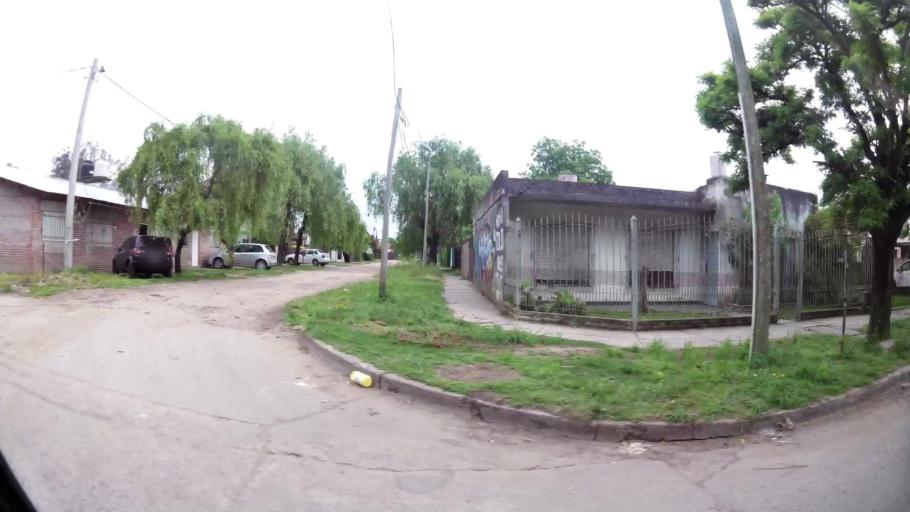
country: AR
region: Buenos Aires
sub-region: Partido de Ezeiza
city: Ezeiza
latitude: -34.8642
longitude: -58.5152
